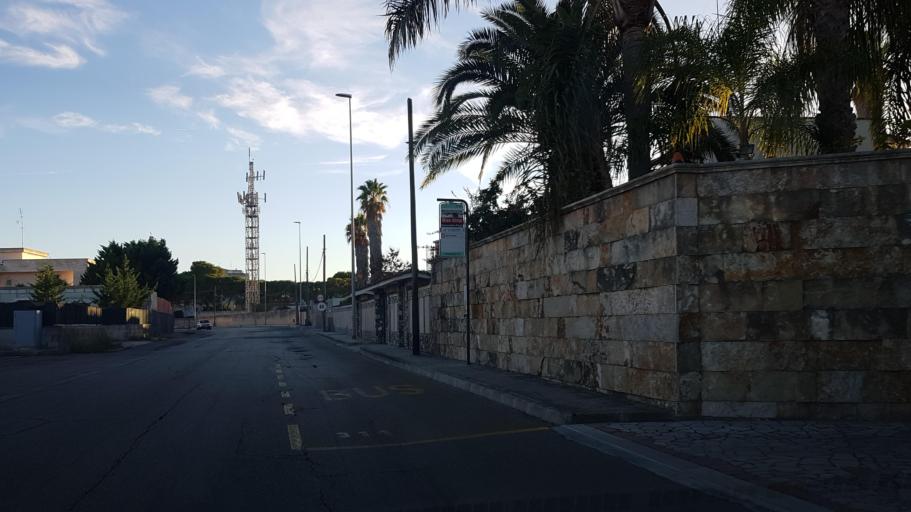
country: IT
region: Apulia
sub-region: Provincia di Lecce
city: Lecce
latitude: 40.3702
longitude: 18.1775
